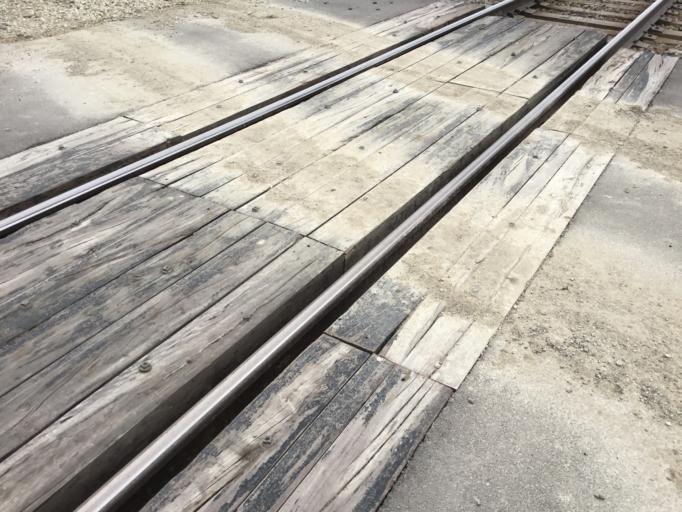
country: US
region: Kansas
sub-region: Dickinson County
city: Herington
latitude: 38.7461
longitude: -96.8161
